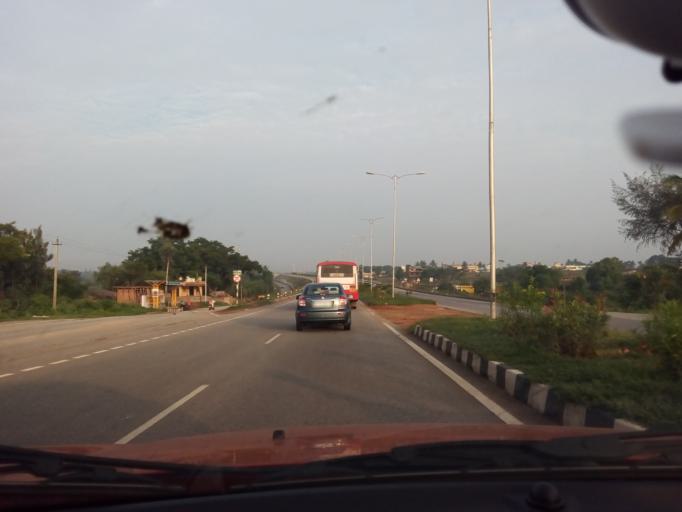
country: IN
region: Karnataka
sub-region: Ramanagara
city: Magadi
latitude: 13.0634
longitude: 77.2746
